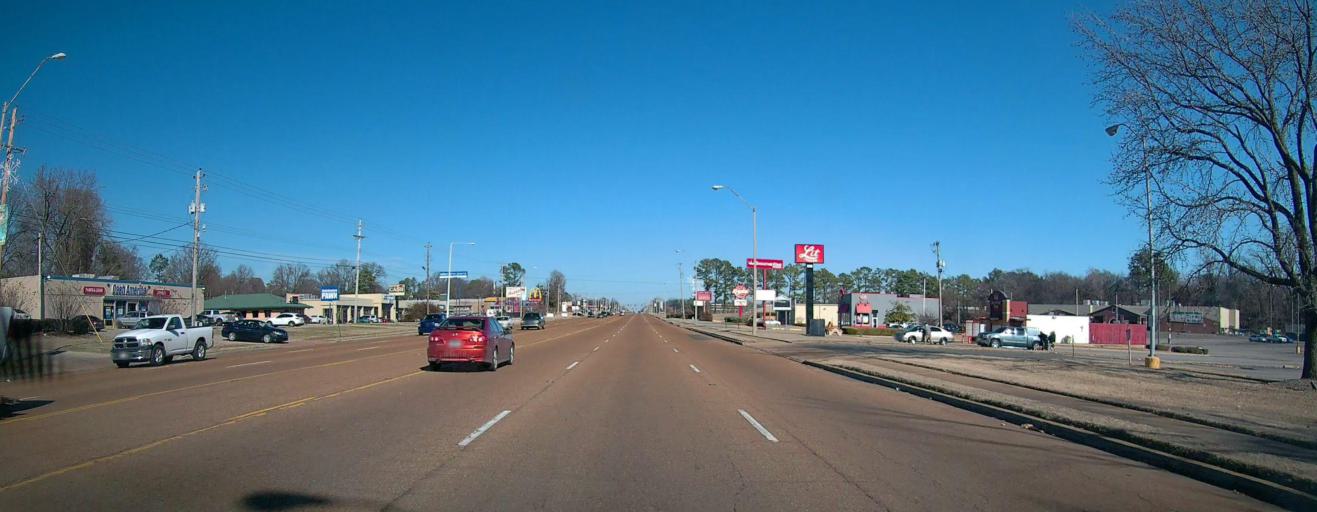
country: US
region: Tennessee
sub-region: Shelby County
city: Bartlett
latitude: 35.2149
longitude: -89.9153
